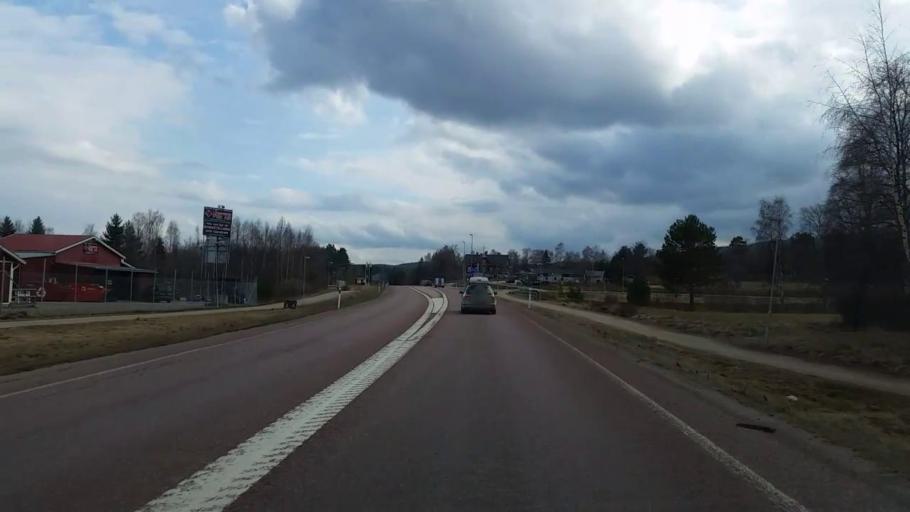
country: SE
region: Gaevleborg
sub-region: Ljusdals Kommun
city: Jaervsoe
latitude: 61.6737
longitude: 16.1449
